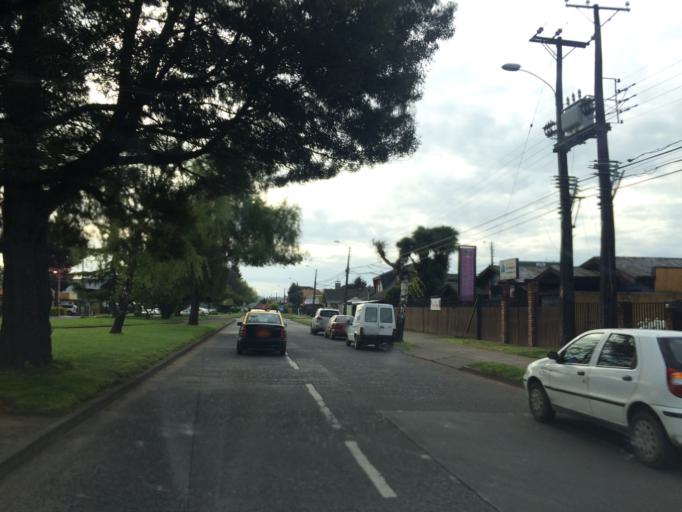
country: CL
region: Araucania
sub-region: Provincia de Cautin
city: Temuco
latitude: -38.7397
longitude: -72.6232
